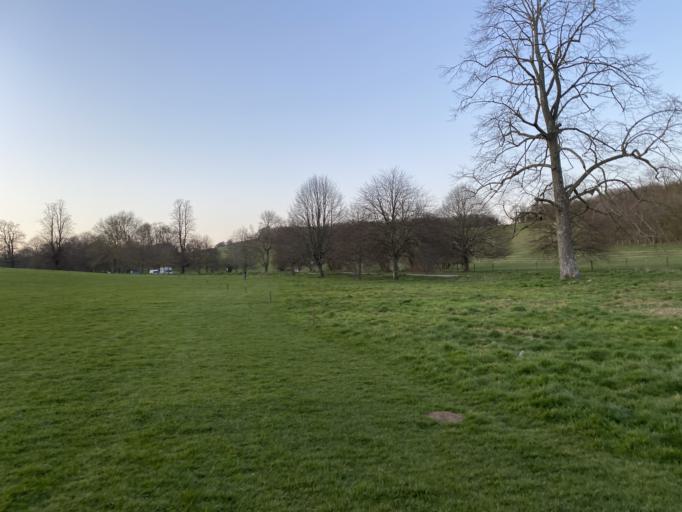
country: GB
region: England
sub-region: Brighton and Hove
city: Brighton
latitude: 50.8661
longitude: -0.0973
